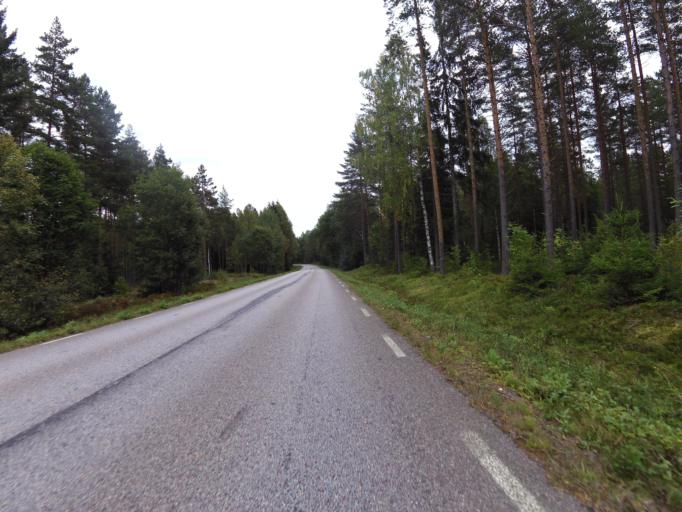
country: SE
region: Gaevleborg
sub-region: Sandvikens Kommun
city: Sandviken
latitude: 60.6609
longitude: 16.8611
